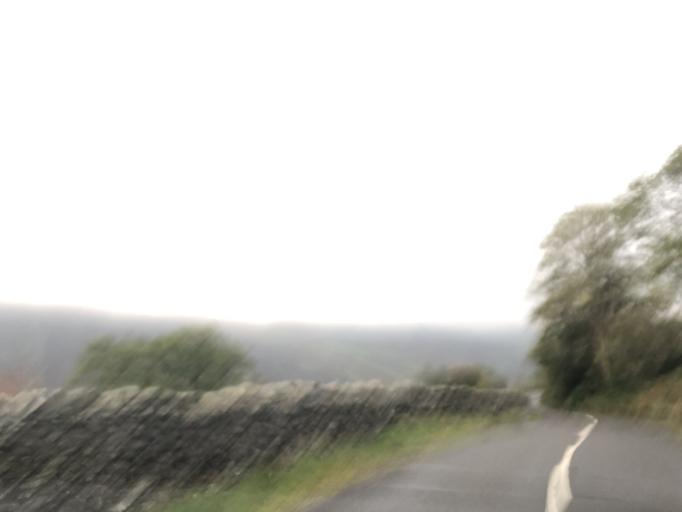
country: GB
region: England
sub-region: Cumbria
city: Ambleside
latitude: 54.4464
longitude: -2.9039
